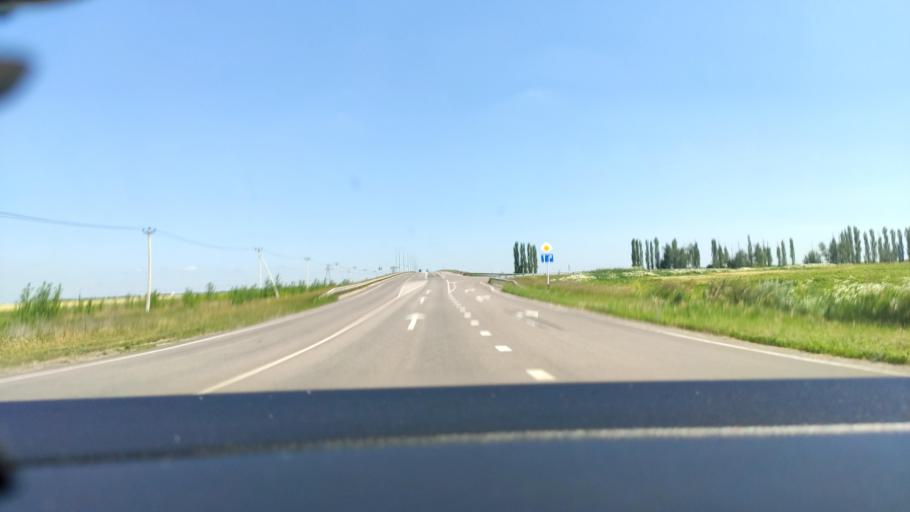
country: RU
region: Voronezj
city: Novaya Usman'
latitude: 51.5853
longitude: 39.3746
